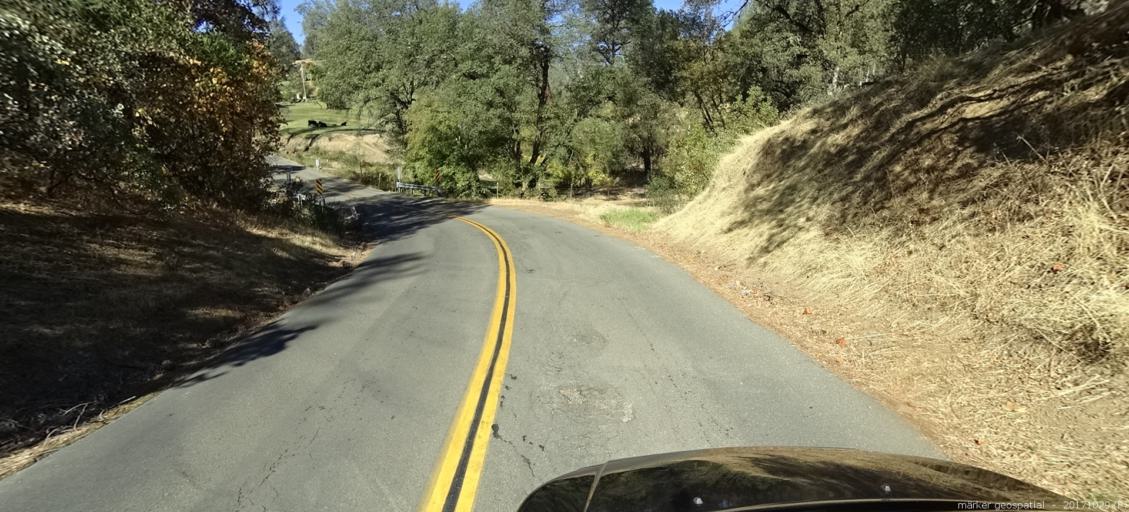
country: US
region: California
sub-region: Shasta County
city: Shasta
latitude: 40.4763
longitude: -122.6252
